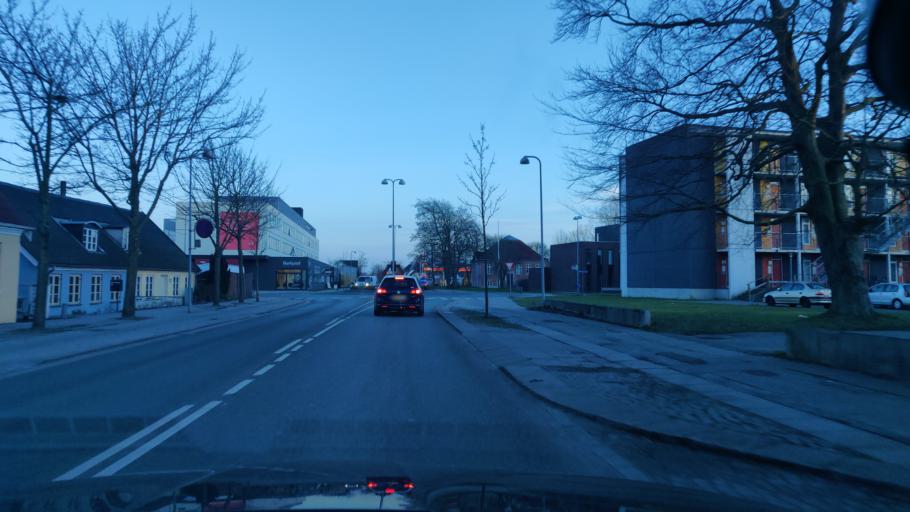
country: DK
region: North Denmark
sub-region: Alborg Kommune
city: Aalborg
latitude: 57.0674
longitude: 9.9020
